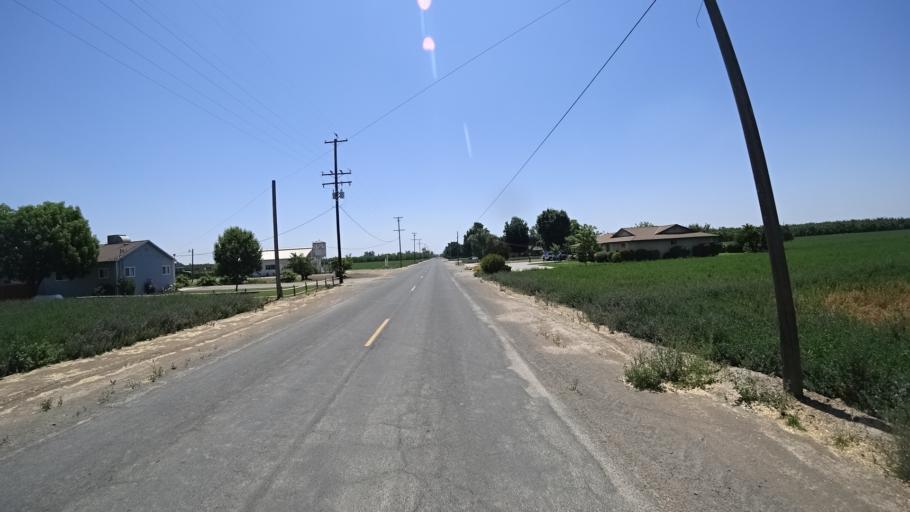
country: US
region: California
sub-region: Kings County
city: Armona
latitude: 36.3352
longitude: -119.7270
